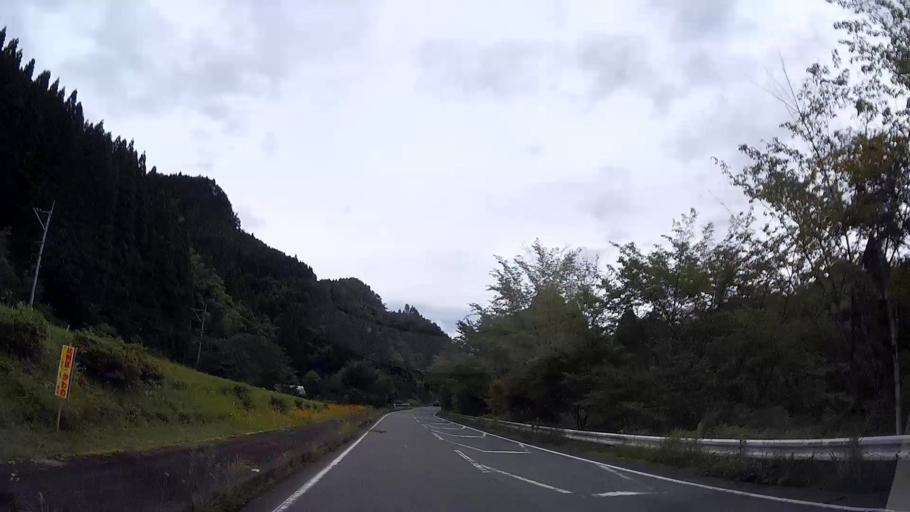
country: JP
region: Oita
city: Hita
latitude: 33.1348
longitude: 130.9867
